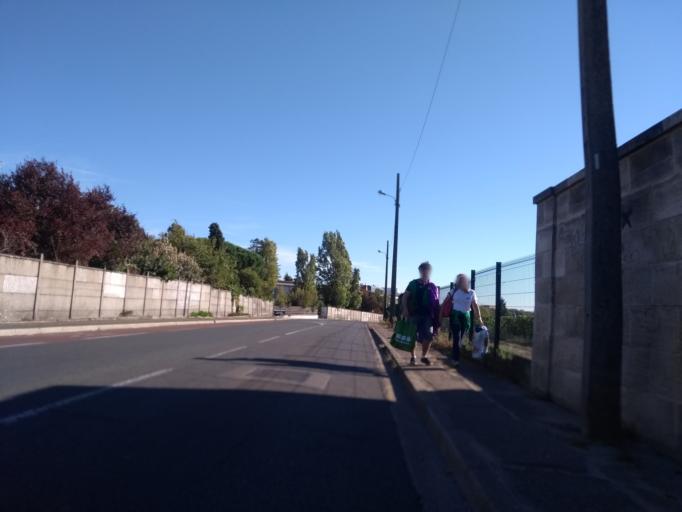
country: FR
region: Aquitaine
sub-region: Departement de la Gironde
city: Talence
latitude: 44.8108
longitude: -0.6004
